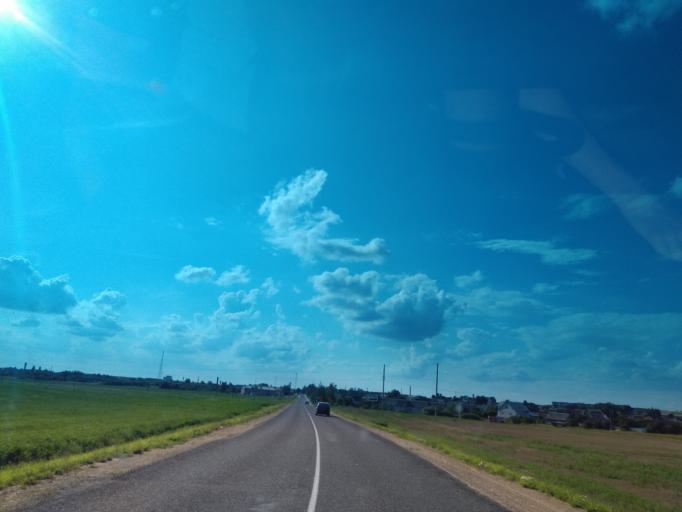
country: BY
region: Minsk
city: Kapyl'
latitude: 53.1411
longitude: 27.1168
